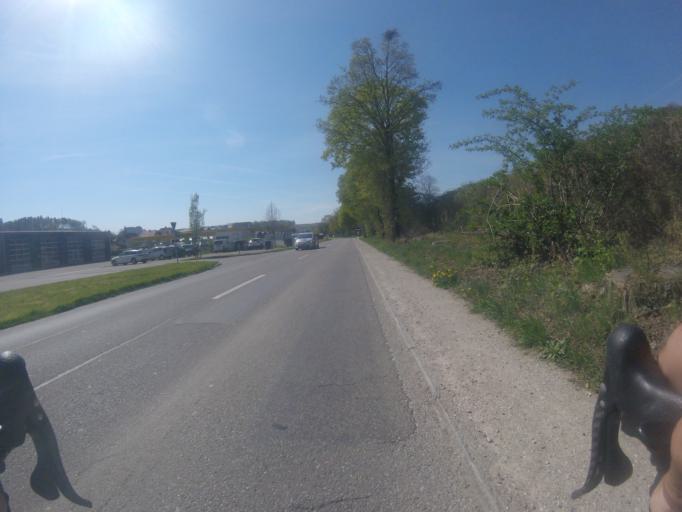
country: CH
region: Bern
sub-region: Bern-Mittelland District
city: Laupen
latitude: 46.9090
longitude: 7.2356
